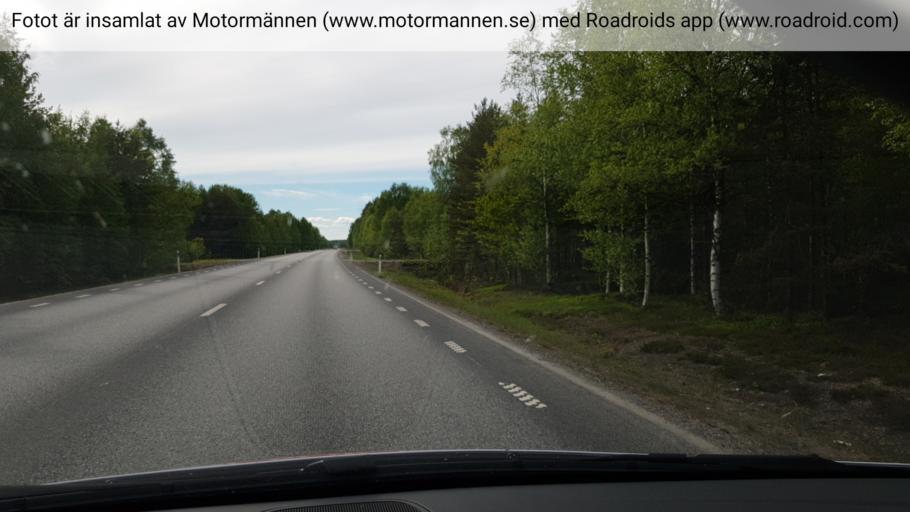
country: SE
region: Vaesterbotten
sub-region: Umea Kommun
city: Roback
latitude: 63.8500
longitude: 20.1197
